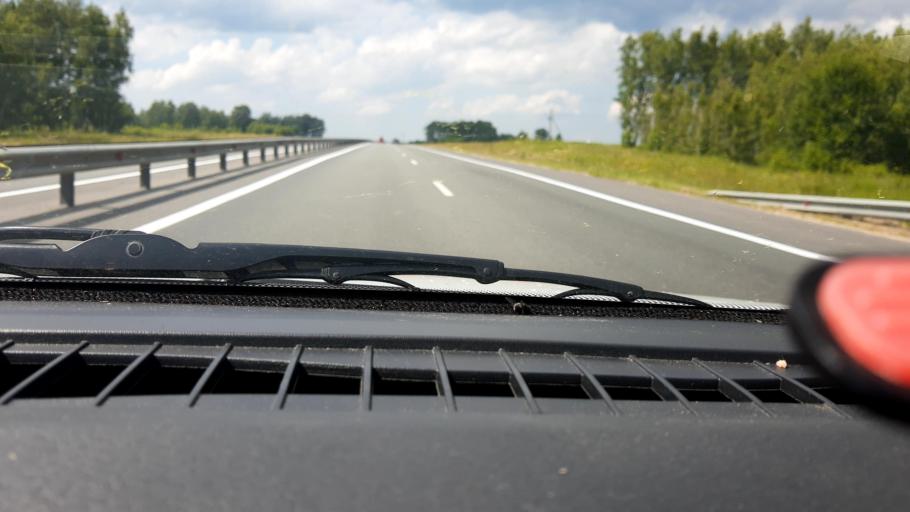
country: RU
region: Nizjnij Novgorod
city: Kstovo
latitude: 56.0863
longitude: 44.0894
